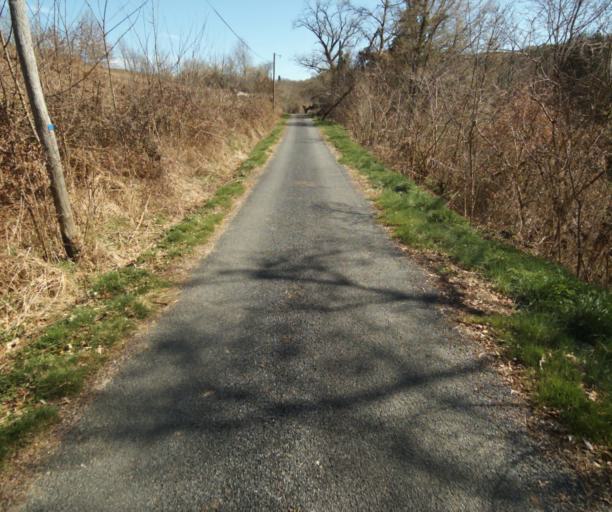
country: FR
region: Limousin
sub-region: Departement de la Correze
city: Chamboulive
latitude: 45.4395
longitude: 1.7285
